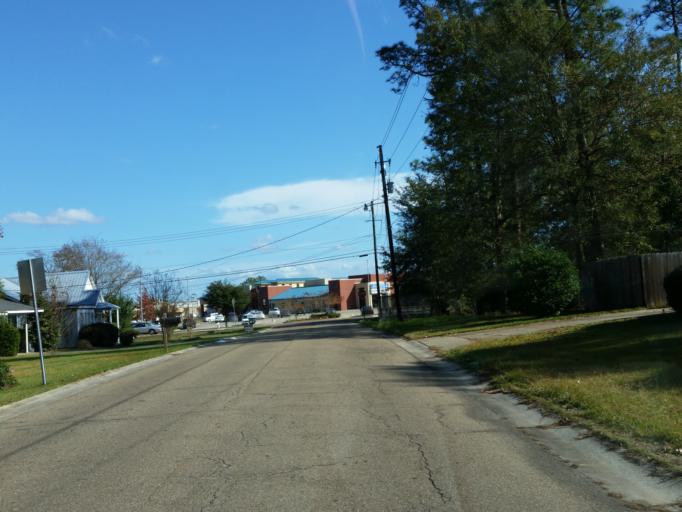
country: US
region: Mississippi
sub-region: Forrest County
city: Hattiesburg
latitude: 31.3100
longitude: -89.3225
